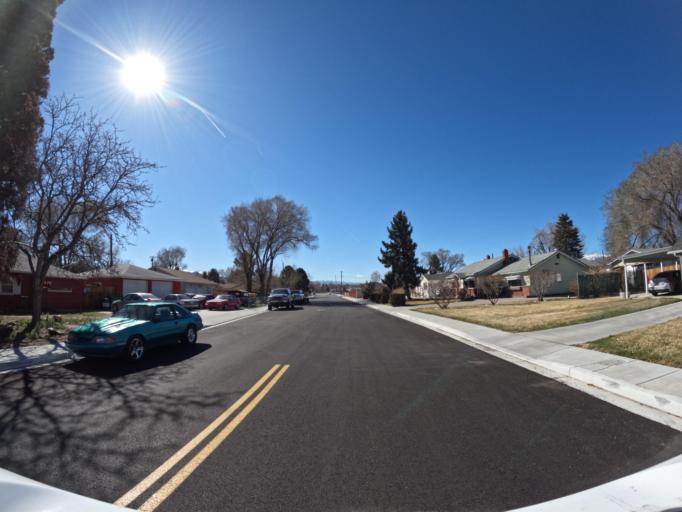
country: US
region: Nevada
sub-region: Washoe County
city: Sparks
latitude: 39.5435
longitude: -119.7456
